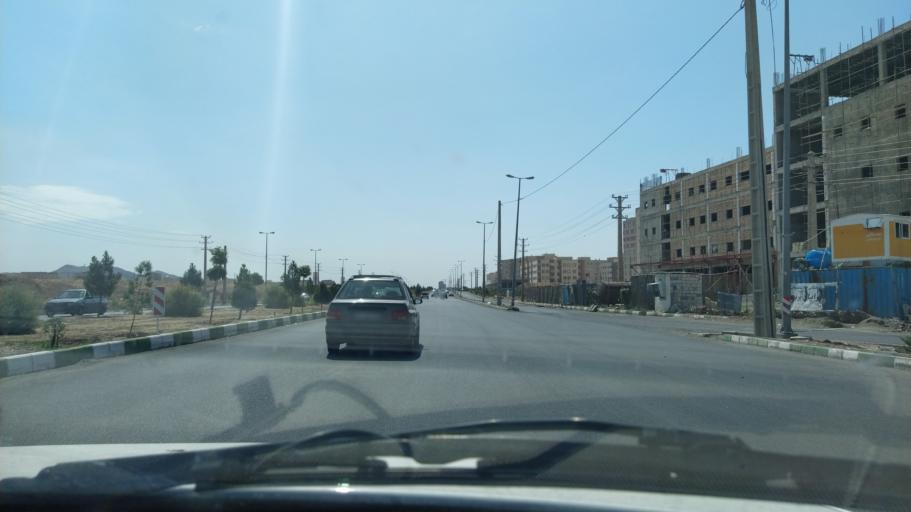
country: IR
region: Tehran
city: Robat Karim
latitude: 35.4889
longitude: 50.9201
